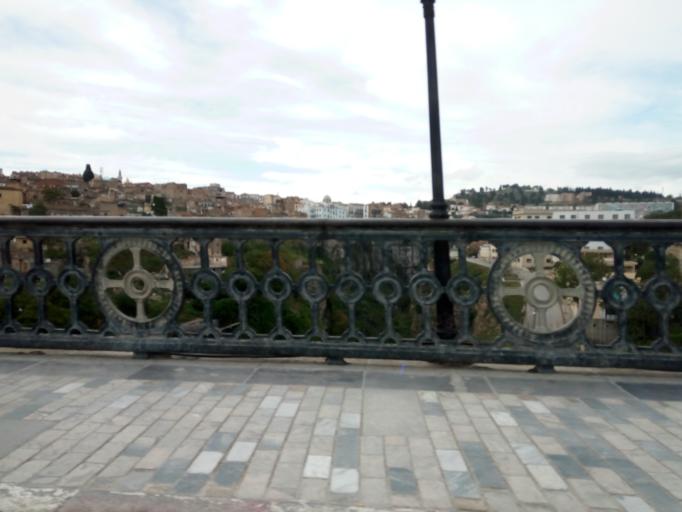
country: DZ
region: Constantine
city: Constantine
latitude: 36.3622
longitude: 6.6148
